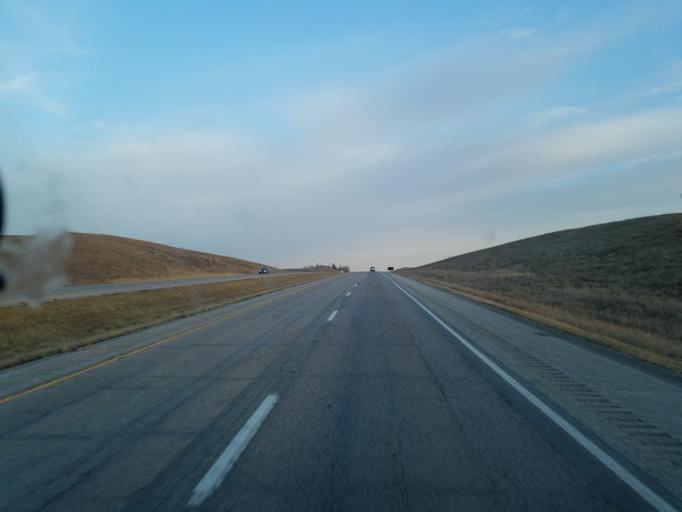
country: US
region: Iowa
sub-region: Harrison County
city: Missouri Valley
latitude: 41.4995
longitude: -95.7838
